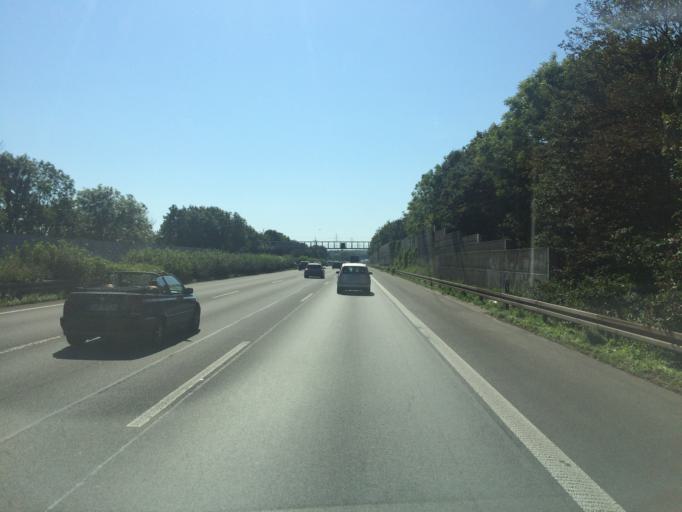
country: DE
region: North Rhine-Westphalia
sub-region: Regierungsbezirk Arnsberg
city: Unna
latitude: 51.5499
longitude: 7.6635
